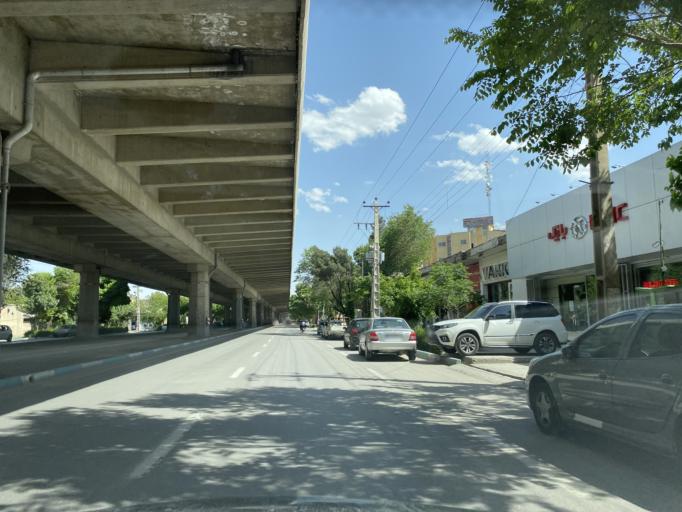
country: IR
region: Isfahan
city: Rehnan
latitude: 32.6908
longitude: 51.6292
